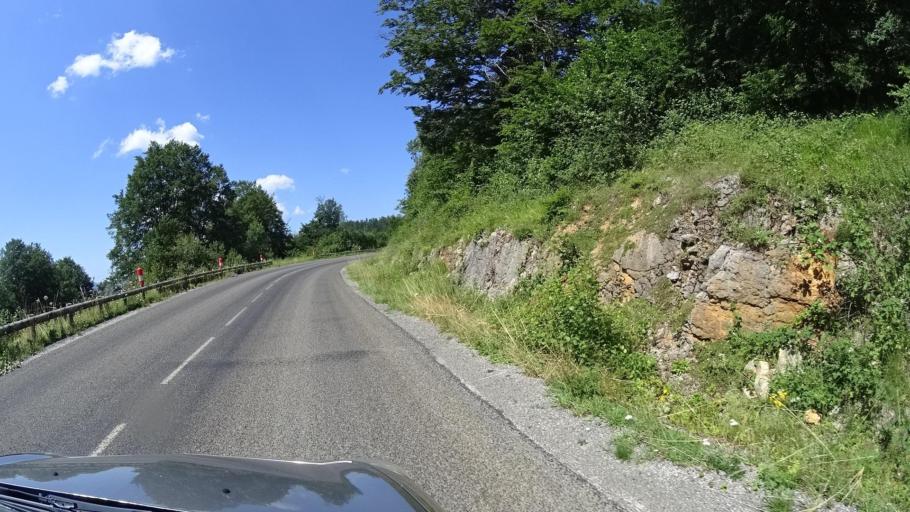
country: FR
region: Franche-Comte
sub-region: Departement du Jura
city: Longchaumois
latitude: 46.5051
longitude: 5.9428
